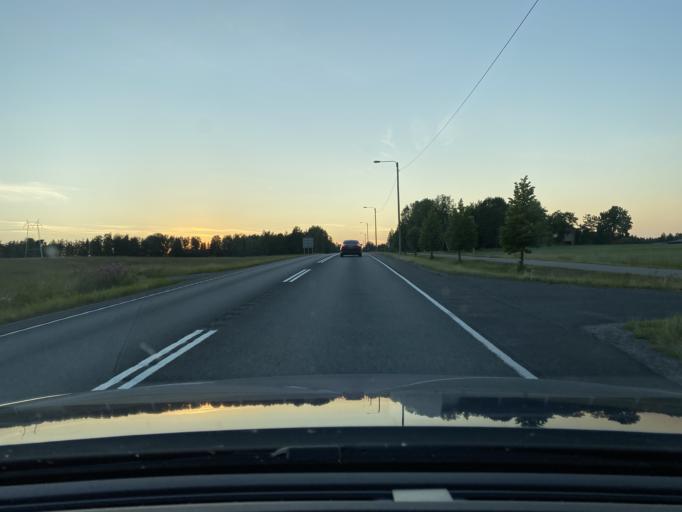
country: FI
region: Pirkanmaa
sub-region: Luoteis-Pirkanmaa
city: Ikaalinen
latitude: 61.7617
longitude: 23.0241
